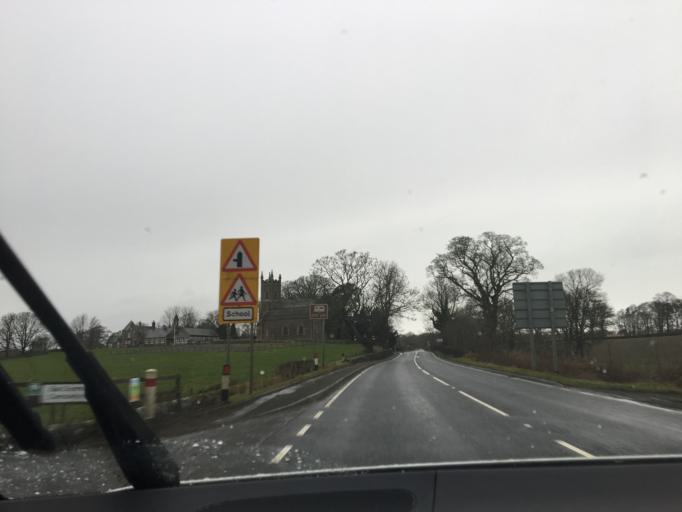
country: GB
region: Scotland
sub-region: Stirling
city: Doune
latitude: 56.1639
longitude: -4.0622
